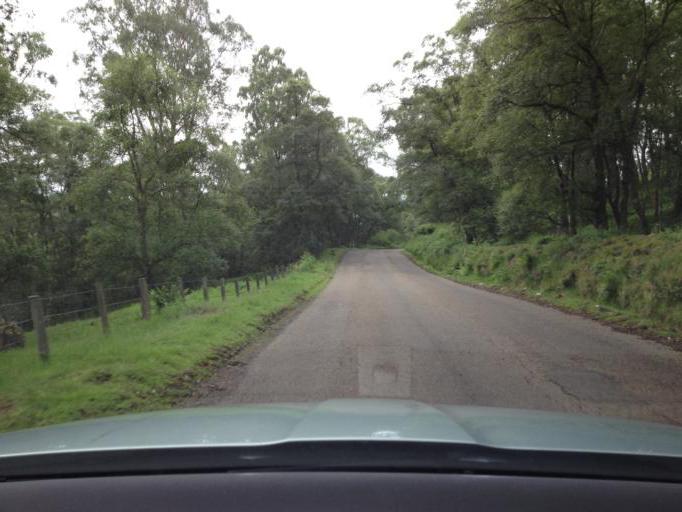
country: GB
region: Scotland
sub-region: Aberdeenshire
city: Aboyne
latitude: 56.8938
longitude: -2.7701
